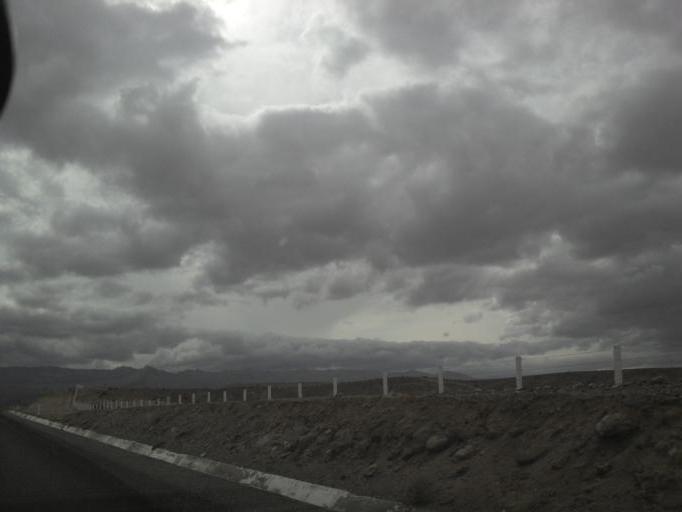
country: MX
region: Baja California
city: Progreso
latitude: 32.5651
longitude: -115.8637
